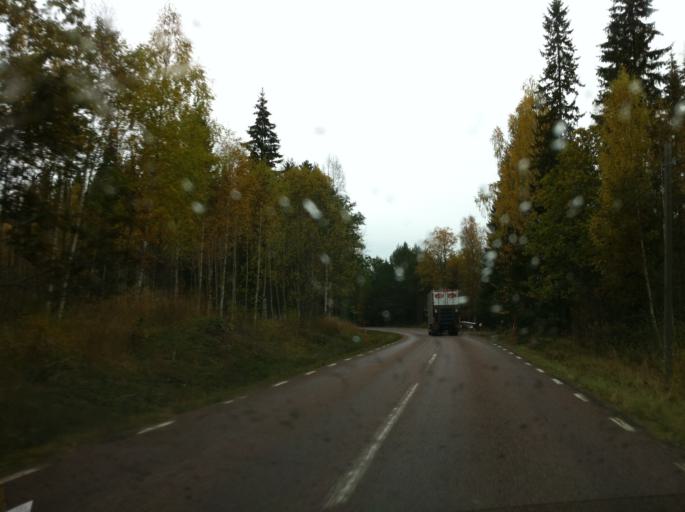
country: SE
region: Dalarna
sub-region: Ludvika Kommun
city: Grangesberg
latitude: 60.1768
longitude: 14.9770
